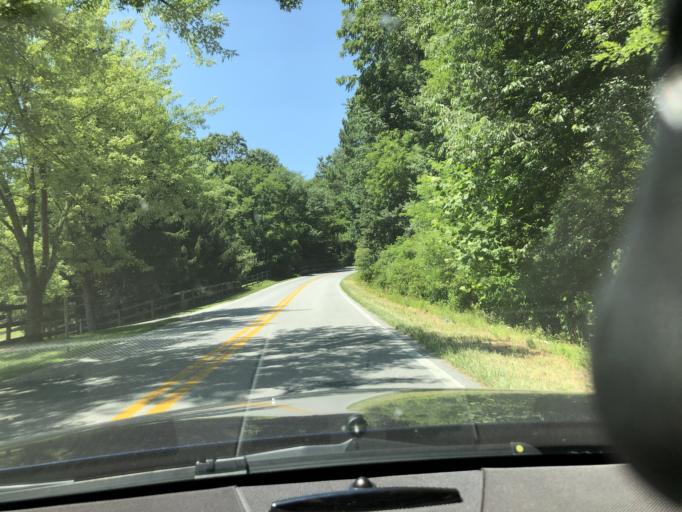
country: US
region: Maryland
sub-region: Carroll County
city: Westminster
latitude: 39.5097
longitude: -76.9279
